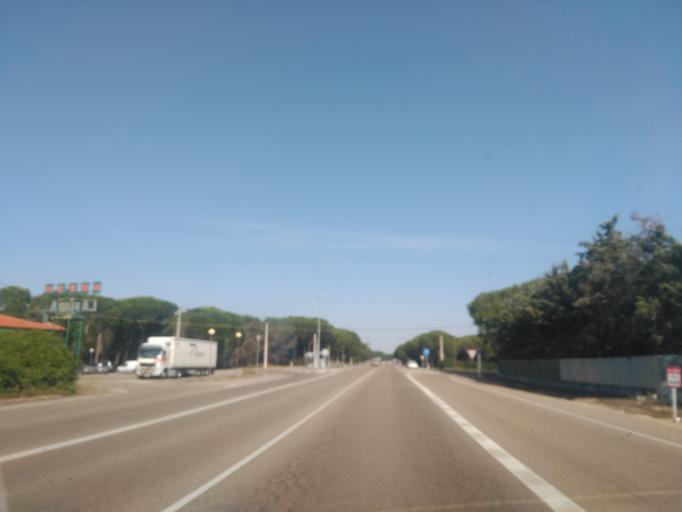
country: ES
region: Castille and Leon
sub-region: Provincia de Valladolid
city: Villabanez
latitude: 41.5944
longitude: -4.5192
